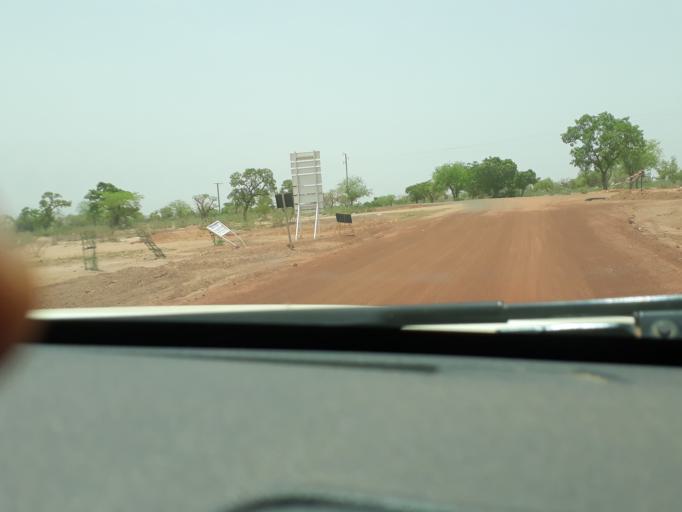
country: BF
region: Plateau-Central
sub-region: Province d'Oubritenga
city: Ziniare
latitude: 12.5788
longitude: -1.3310
